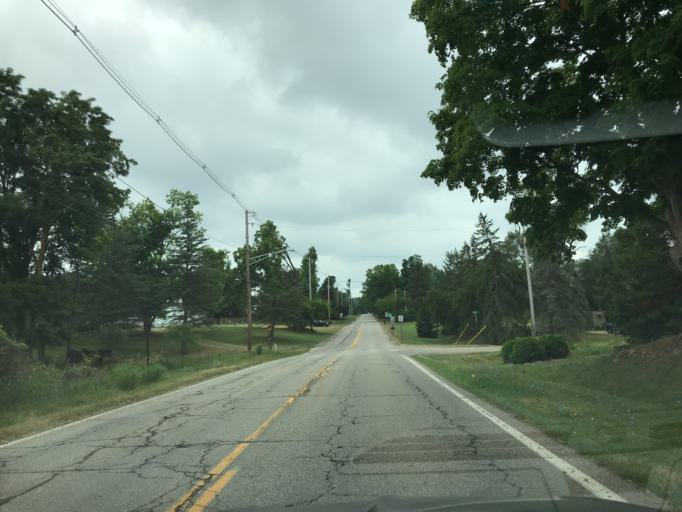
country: US
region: Michigan
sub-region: Eaton County
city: Waverly
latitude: 42.7705
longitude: -84.6475
